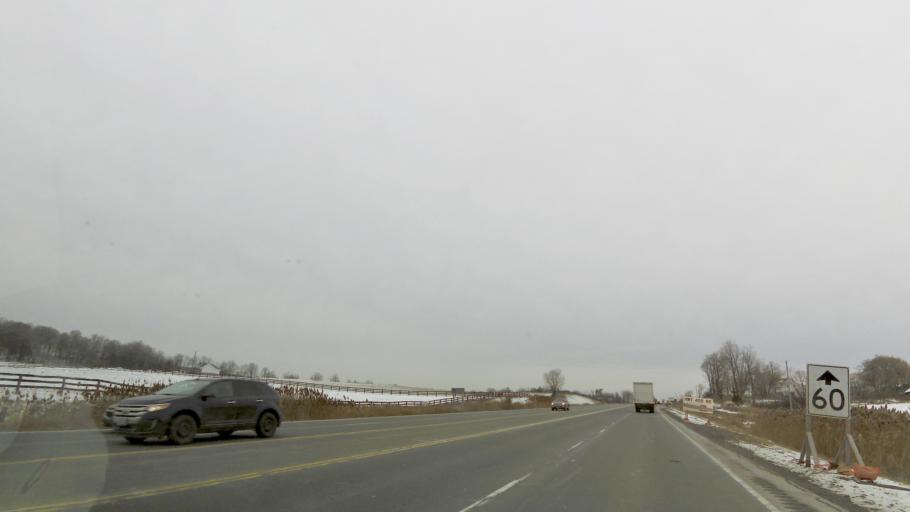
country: CA
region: Ontario
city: Bradford West Gwillimbury
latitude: 44.0317
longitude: -79.5831
